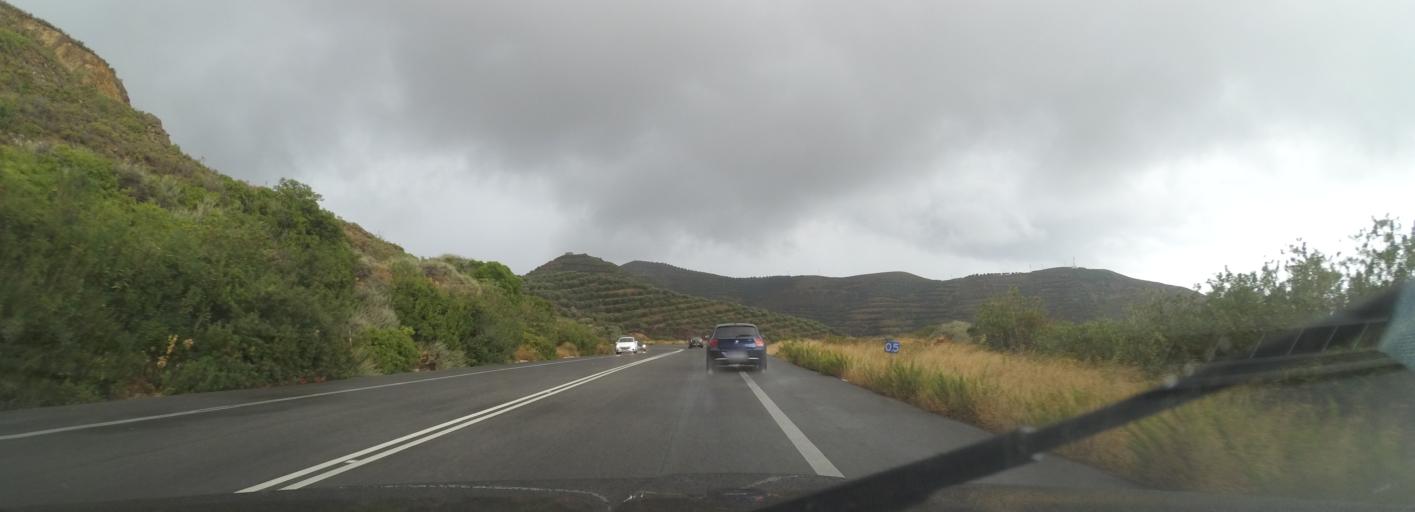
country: GR
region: Crete
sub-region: Nomos Rethymnis
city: Anogeia
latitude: 35.3921
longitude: 24.9015
